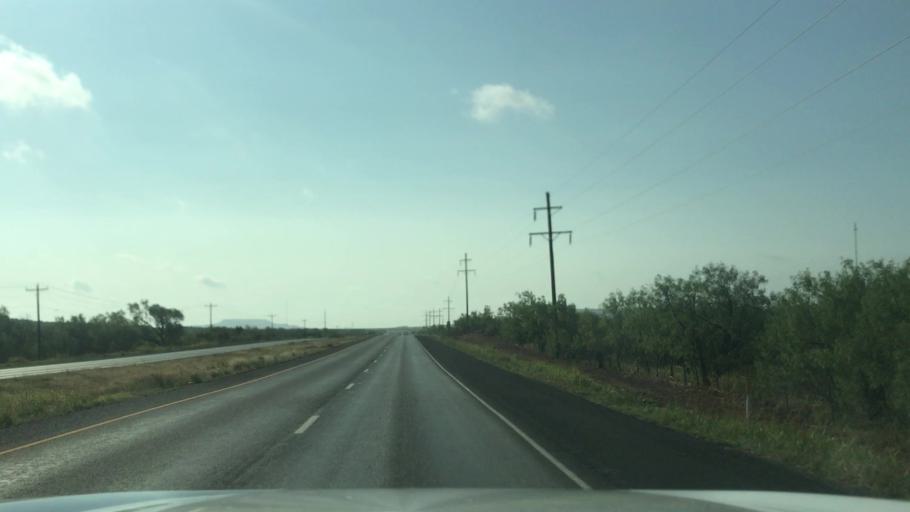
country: US
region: Texas
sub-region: Garza County
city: Post
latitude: 32.9991
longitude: -101.1572
